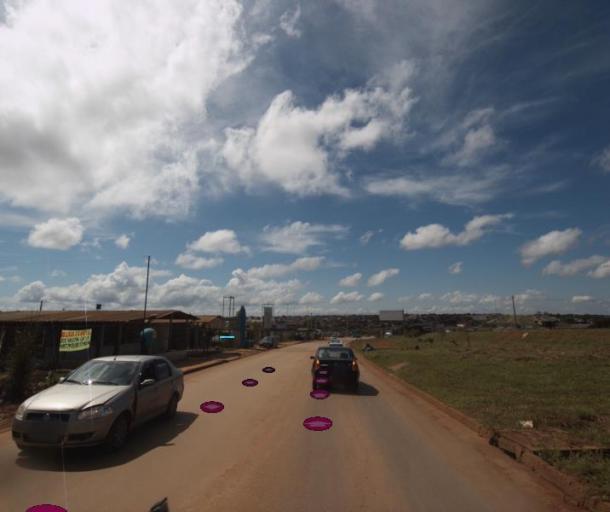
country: BR
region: Federal District
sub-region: Brasilia
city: Brasilia
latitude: -15.7356
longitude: -48.2763
